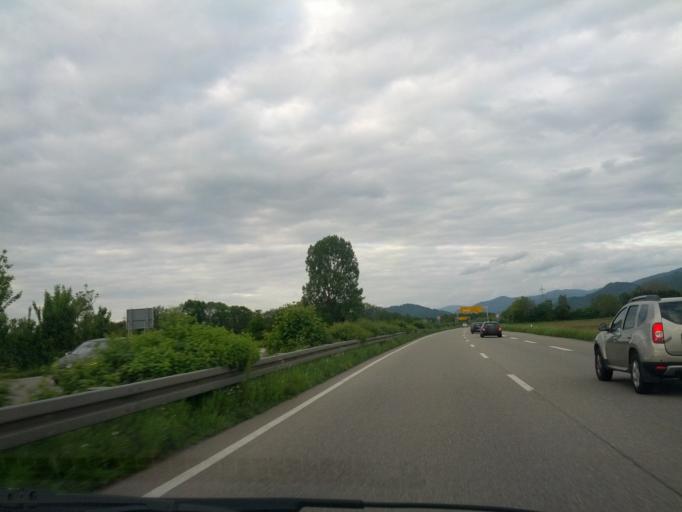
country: DE
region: Baden-Wuerttemberg
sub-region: Freiburg Region
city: Gundelfingen
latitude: 48.0527
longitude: 7.8624
